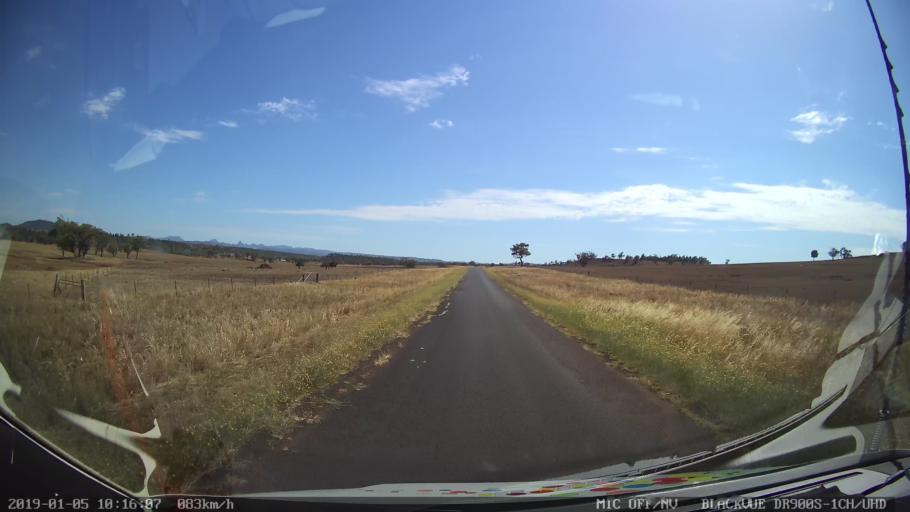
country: AU
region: New South Wales
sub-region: Gilgandra
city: Gilgandra
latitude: -31.5783
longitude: 148.9496
